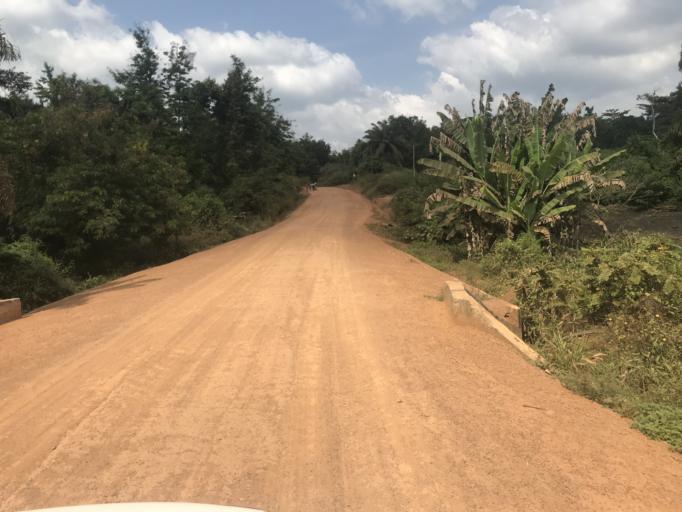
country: NG
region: Osun
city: Inisa
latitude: 7.8575
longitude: 4.3819
